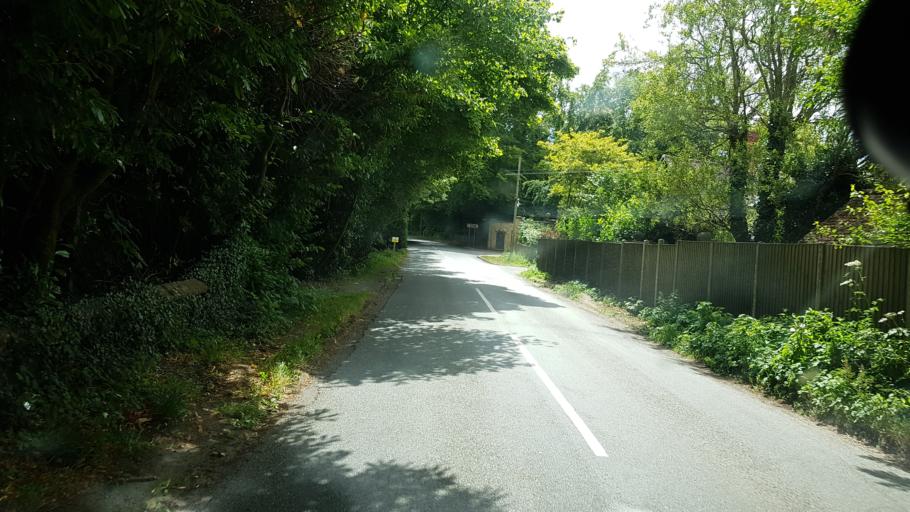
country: GB
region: England
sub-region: West Sussex
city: East Grinstead
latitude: 51.1087
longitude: -0.0285
